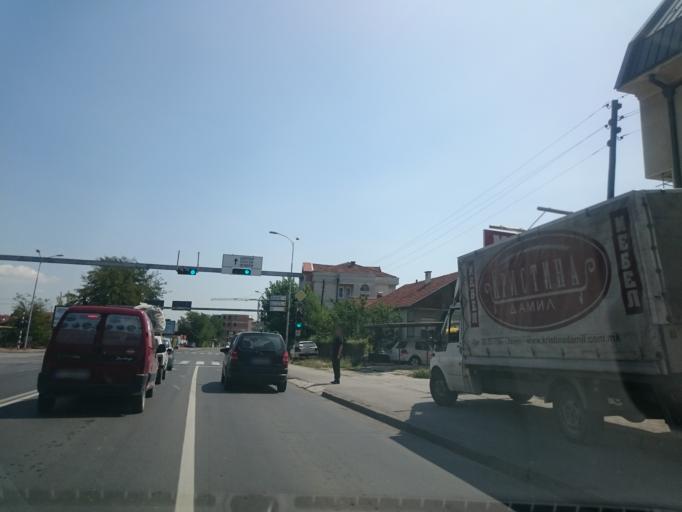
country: MK
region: Saraj
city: Saraj
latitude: 42.0071
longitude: 21.3393
